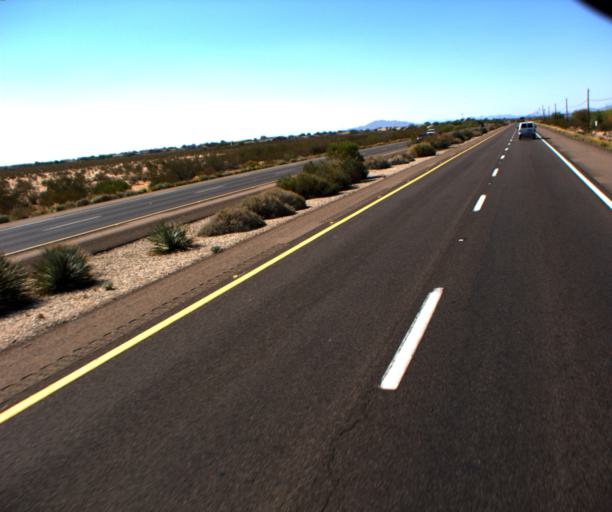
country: US
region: Arizona
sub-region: Pinal County
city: Sacaton
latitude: 32.9872
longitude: -111.7569
